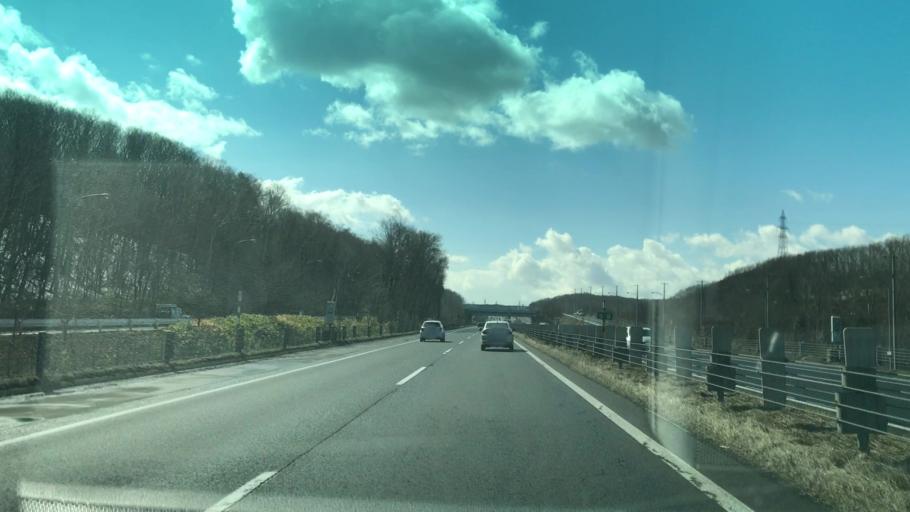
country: JP
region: Hokkaido
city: Kitahiroshima
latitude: 43.0057
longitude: 141.4670
